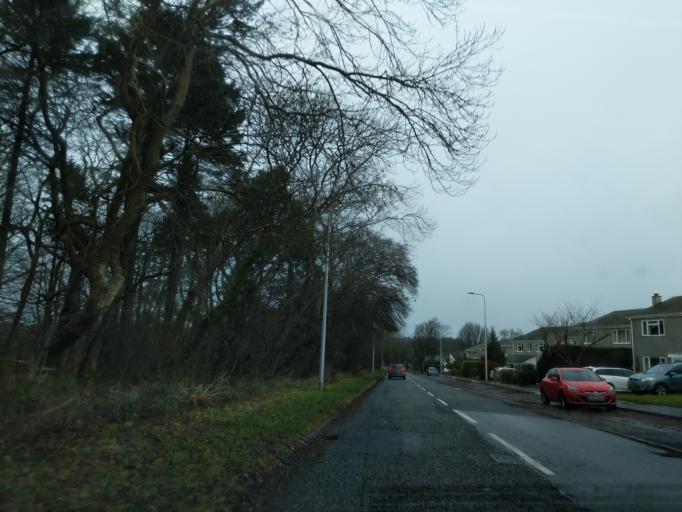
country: GB
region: Scotland
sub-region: Edinburgh
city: Balerno
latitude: 55.8757
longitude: -3.3470
